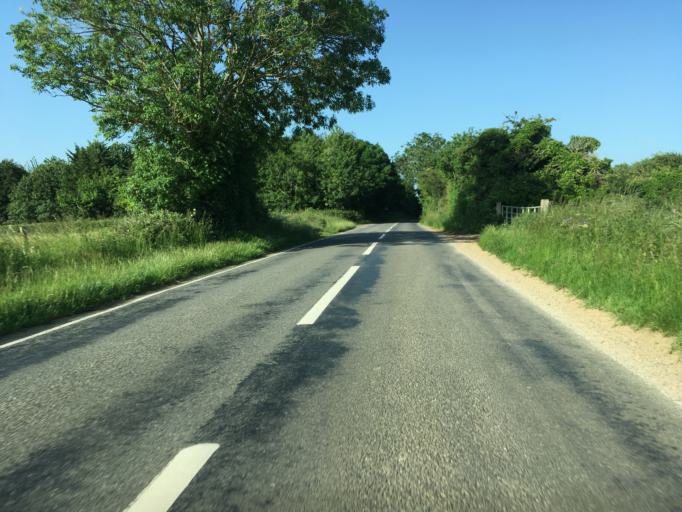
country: GB
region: England
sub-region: Oxfordshire
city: Shipton under Wychwood
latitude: 51.8542
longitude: -1.5716
